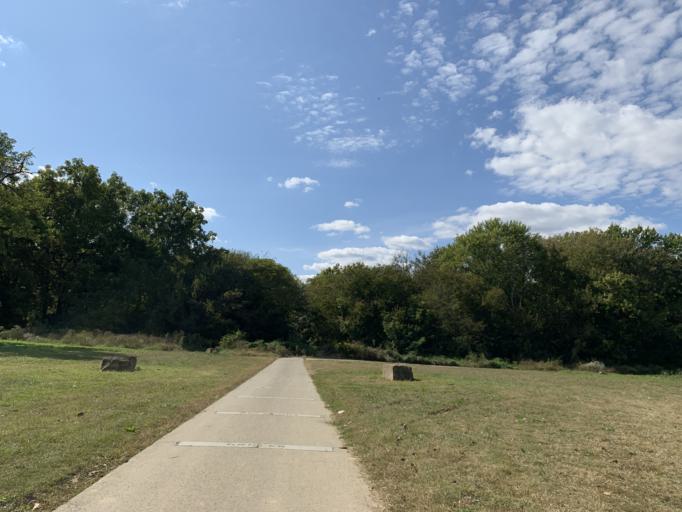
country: US
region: Indiana
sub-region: Floyd County
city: New Albany
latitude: 38.2785
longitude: -85.8025
